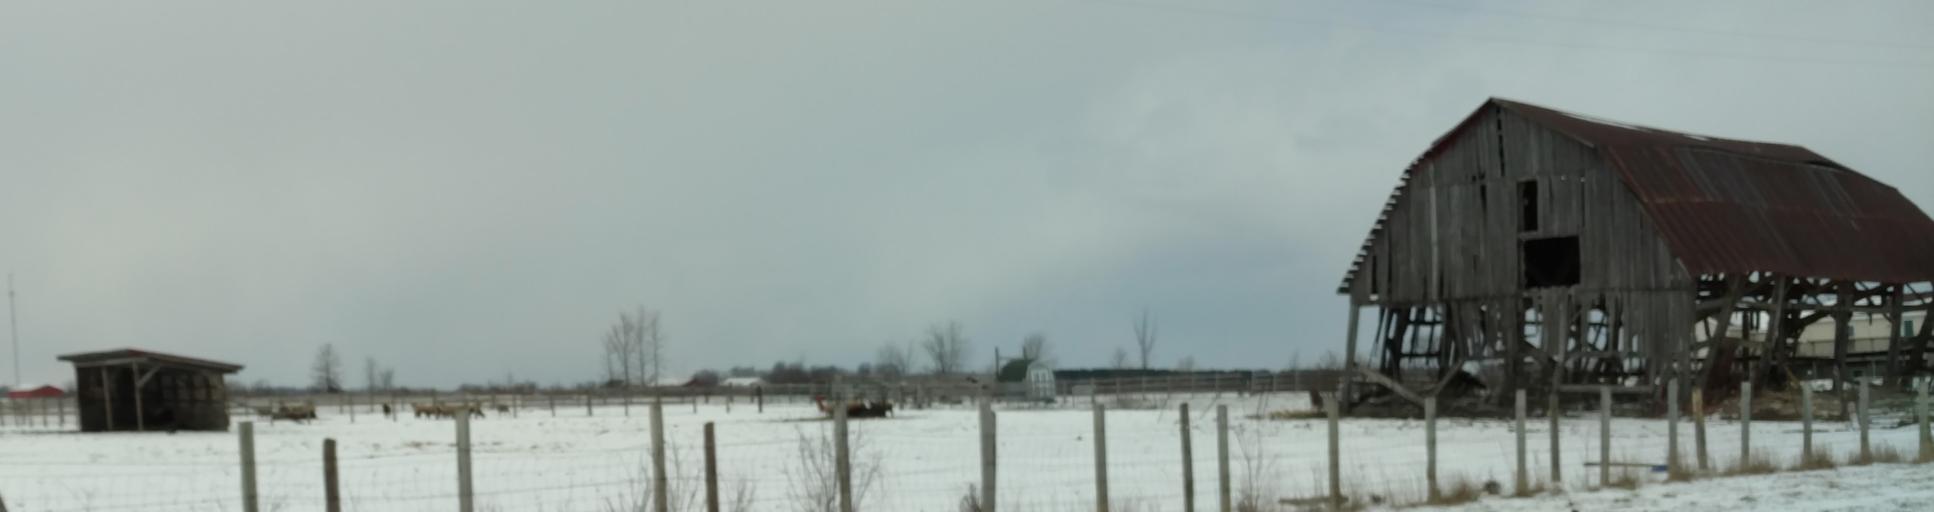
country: US
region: Michigan
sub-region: Gladwin County
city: Gladwin
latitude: 44.0437
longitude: -84.4674
